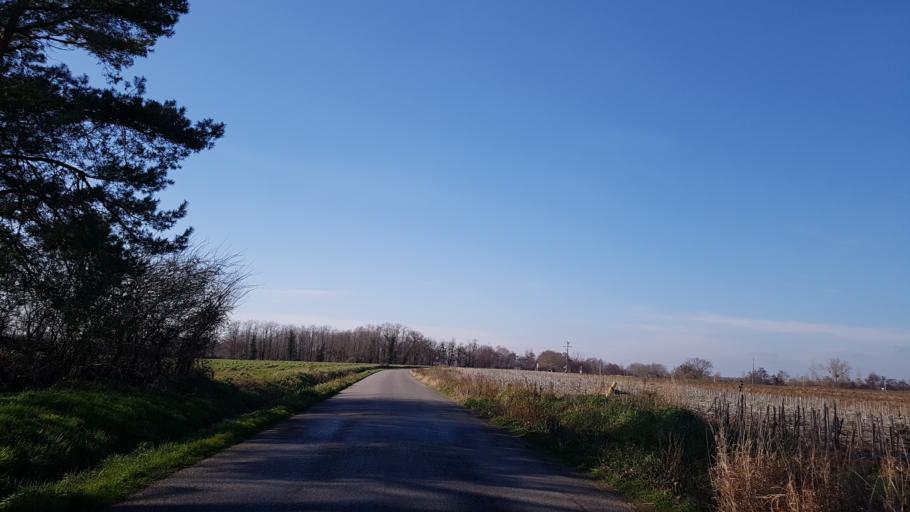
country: FR
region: Midi-Pyrenees
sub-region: Departement de l'Ariege
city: La Tour-du-Crieu
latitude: 43.1434
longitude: 1.7074
